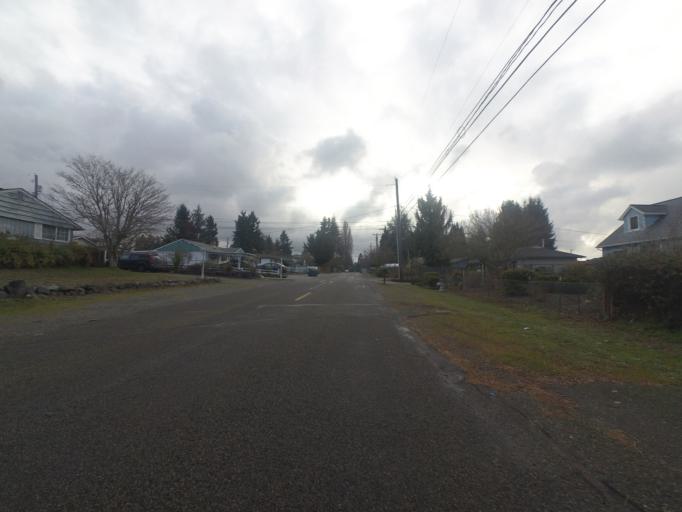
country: US
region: Washington
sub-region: Pierce County
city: University Place
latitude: 47.2400
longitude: -122.5424
